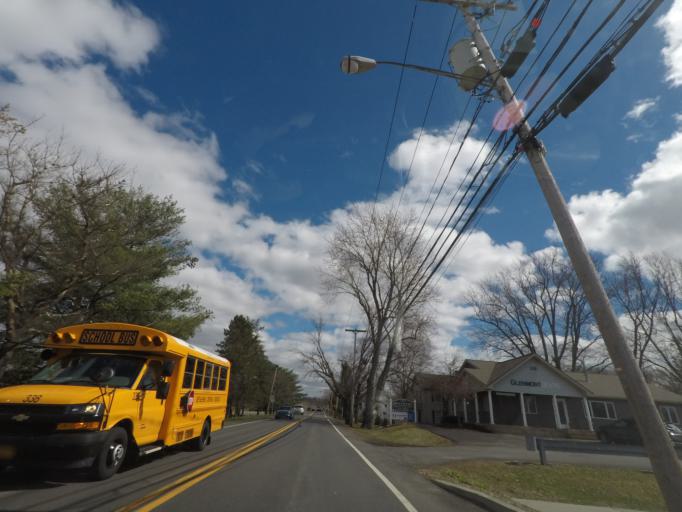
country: US
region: New York
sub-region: Albany County
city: Delmar
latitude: 42.6015
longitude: -73.7910
